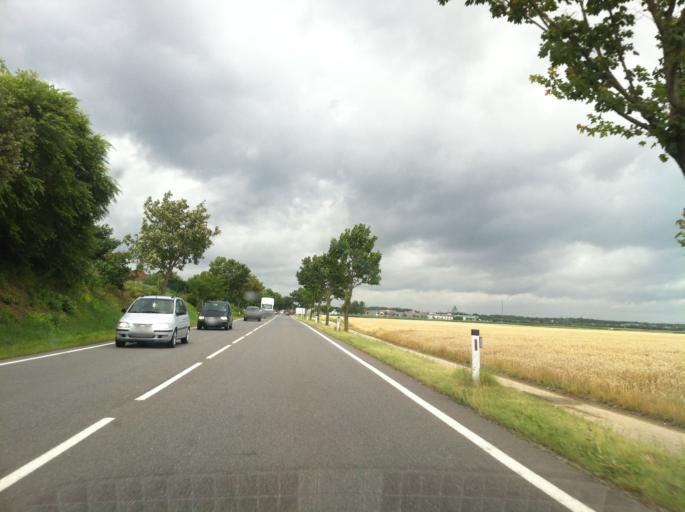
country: AT
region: Lower Austria
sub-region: Politischer Bezirk Tulln
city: Langenrohr
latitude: 48.3053
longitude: 16.0137
